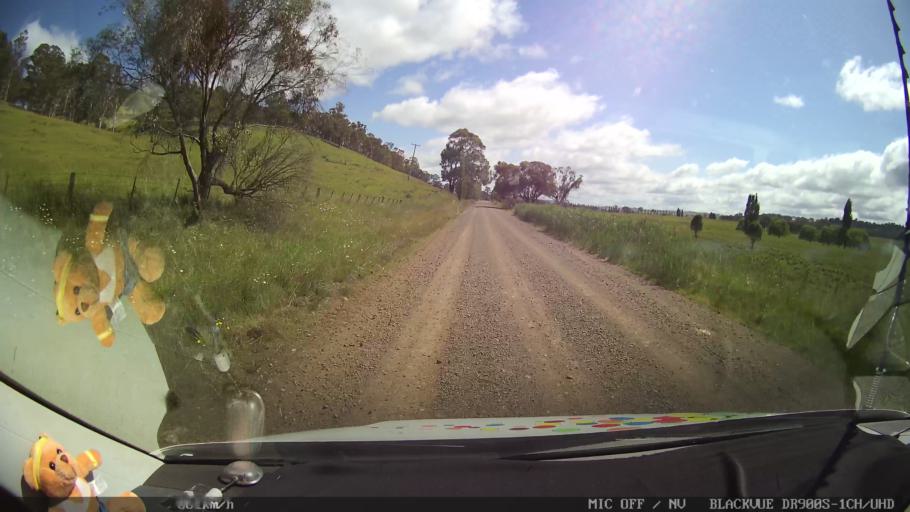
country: AU
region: New South Wales
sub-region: Glen Innes Severn
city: Glen Innes
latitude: -29.9564
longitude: 151.7031
